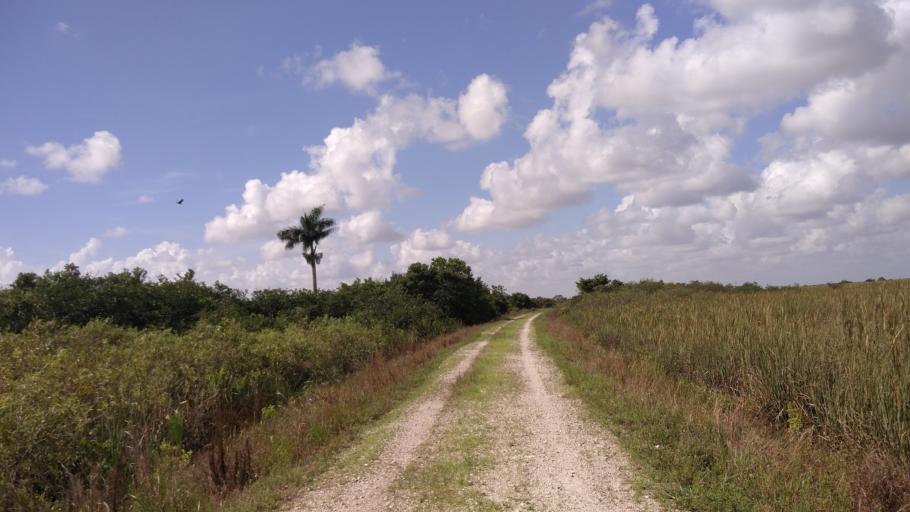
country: US
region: Florida
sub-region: Broward County
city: Weston
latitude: 26.0506
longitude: -80.4614
